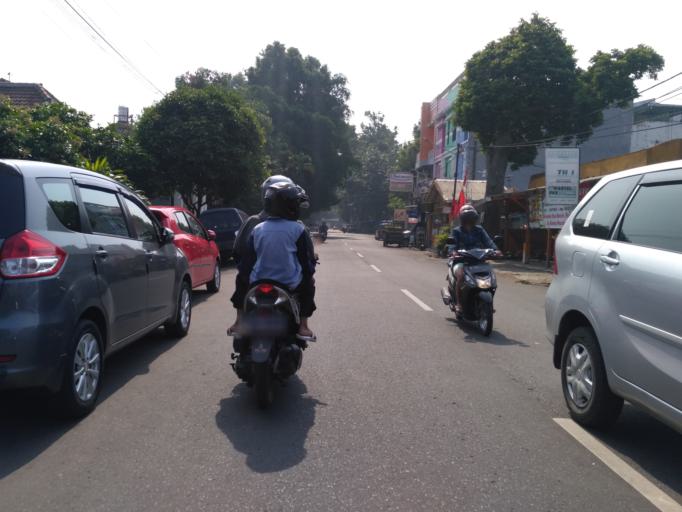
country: ID
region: East Java
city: Malang
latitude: -7.9722
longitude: 112.6351
